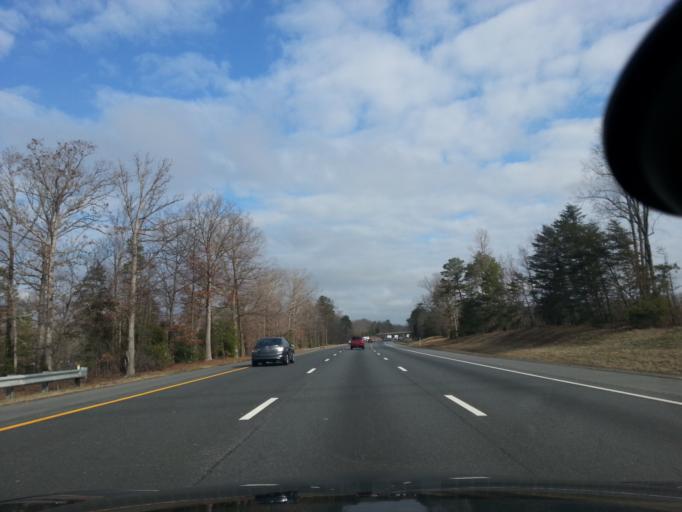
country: US
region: Virginia
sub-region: Spotsylvania County
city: Spotsylvania Courthouse
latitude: 38.0839
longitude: -77.5157
